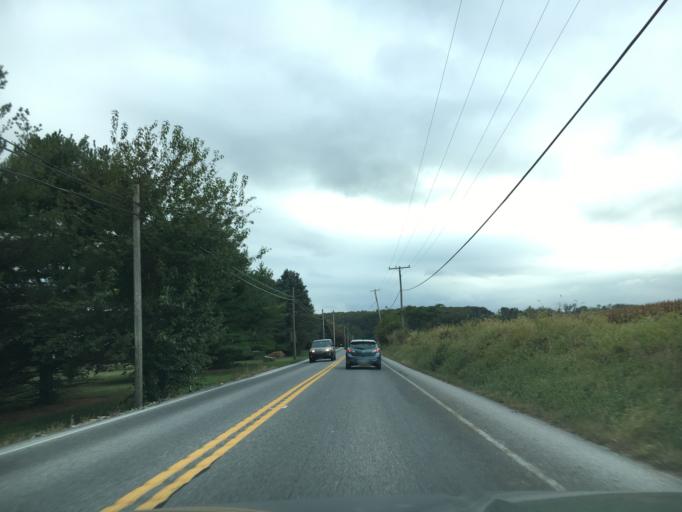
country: US
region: Pennsylvania
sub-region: Lancaster County
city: Quarryville
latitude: 39.8777
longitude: -76.2143
